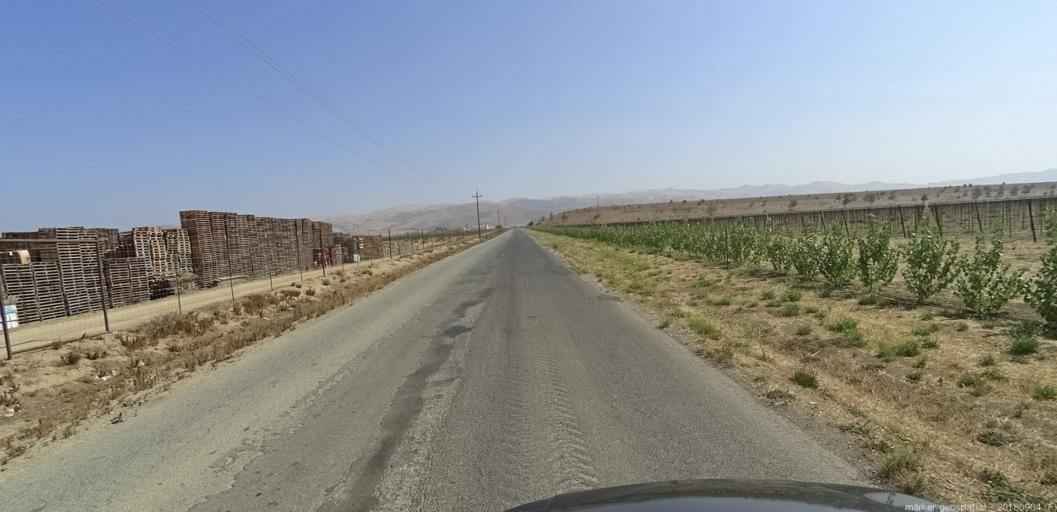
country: US
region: California
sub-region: Monterey County
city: Gonzales
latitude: 36.5282
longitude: -121.4156
